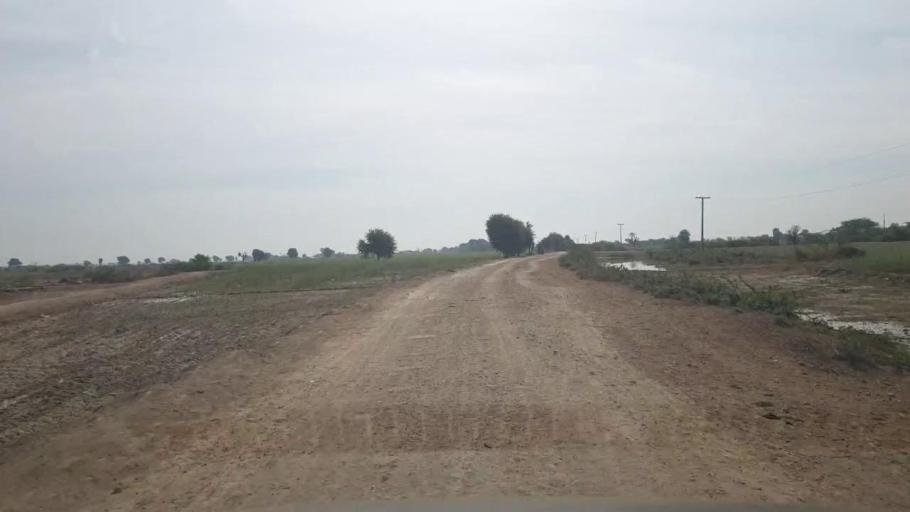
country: PK
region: Sindh
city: Umarkot
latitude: 25.3623
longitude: 69.6256
